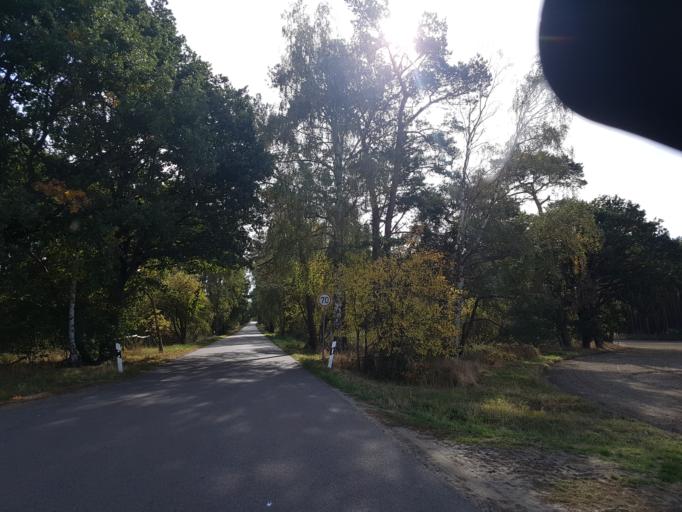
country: DE
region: Brandenburg
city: Schlieben
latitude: 51.7674
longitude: 13.3363
